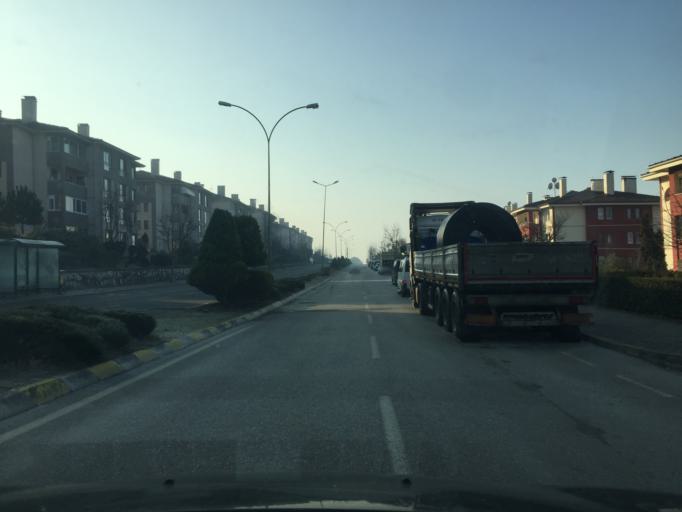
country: TR
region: Duzce
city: Duzce
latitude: 40.8655
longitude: 31.2304
